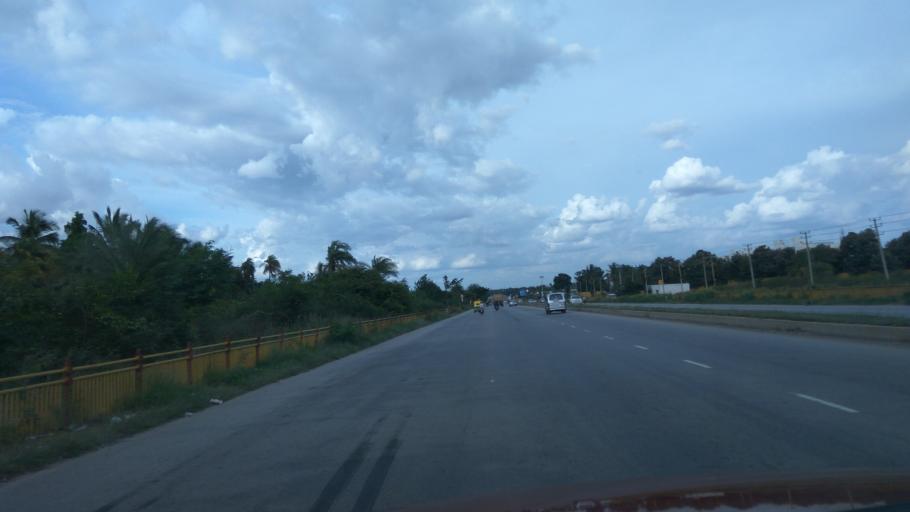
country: IN
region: Karnataka
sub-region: Bangalore Rural
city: Devanhalli
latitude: 13.2282
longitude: 77.6888
